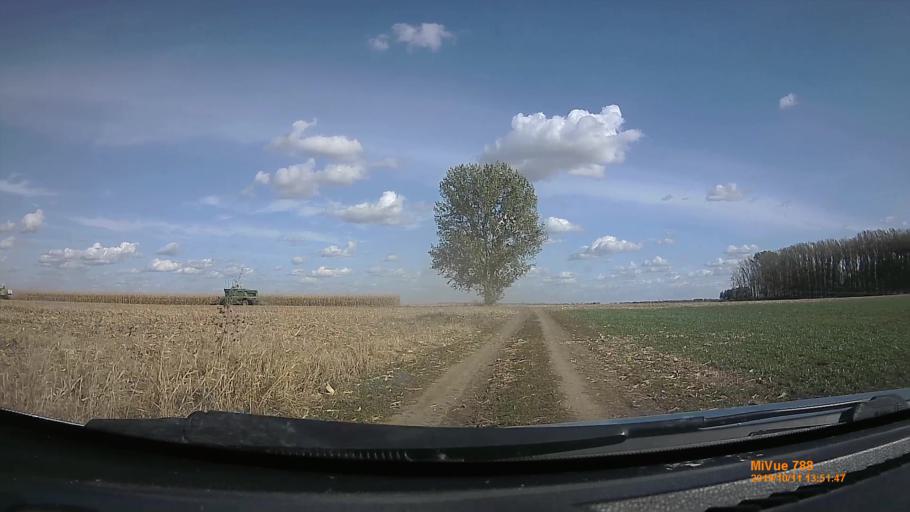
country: HU
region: Hajdu-Bihar
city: Balmazujvaros
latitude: 47.5408
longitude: 21.3984
